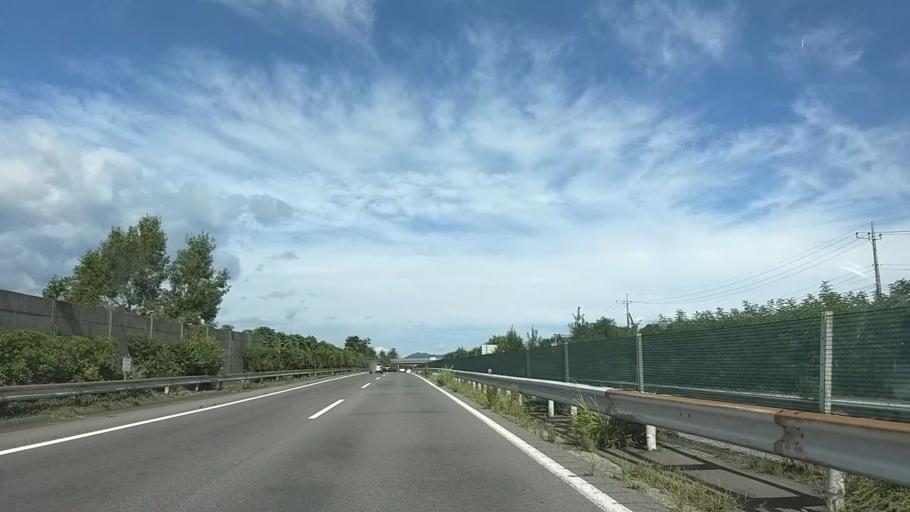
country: JP
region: Yamanashi
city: Nirasaki
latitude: 35.7282
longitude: 138.4600
